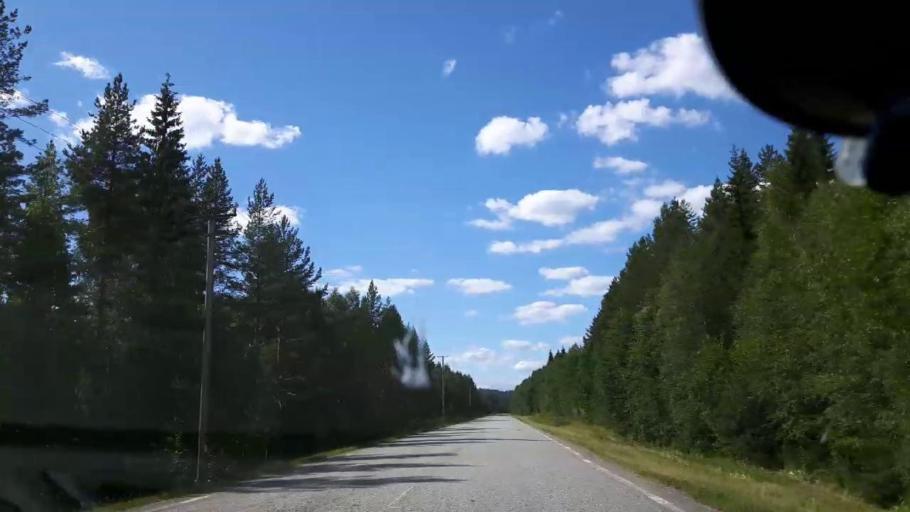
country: SE
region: Vaesternorrland
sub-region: Ange Kommun
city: Fransta
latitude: 62.7625
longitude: 16.2660
